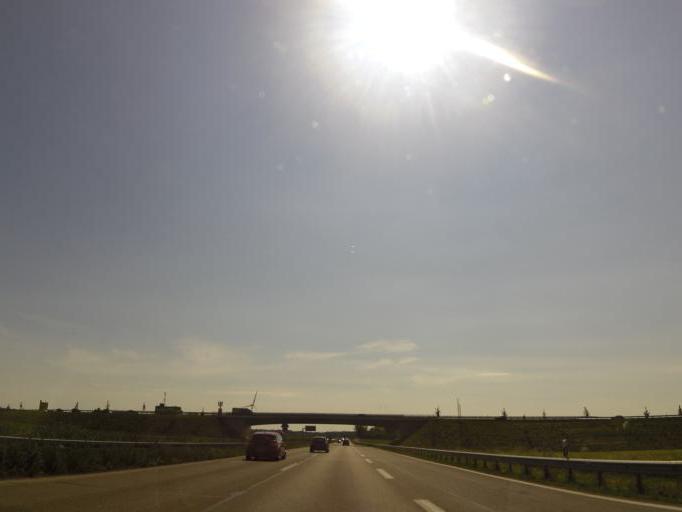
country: DE
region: Baden-Wuerttemberg
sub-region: Tuebingen Region
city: Bernstadt
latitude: 48.4565
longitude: 10.0255
